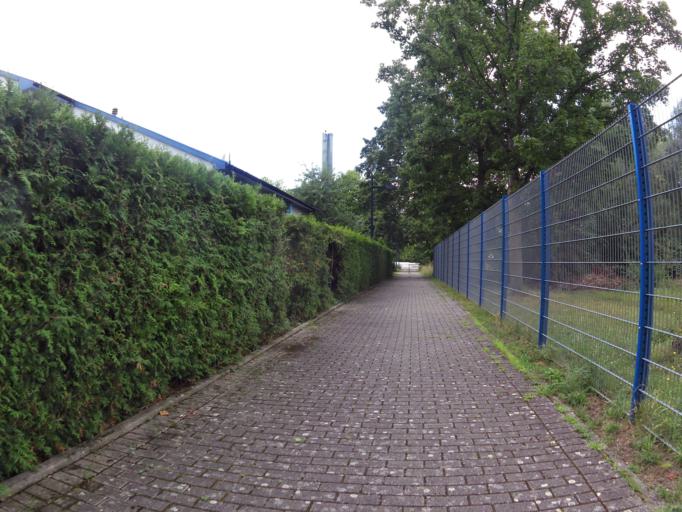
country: DE
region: Baden-Wuerttemberg
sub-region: Freiburg Region
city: Lahr
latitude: 48.3519
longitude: 7.8248
